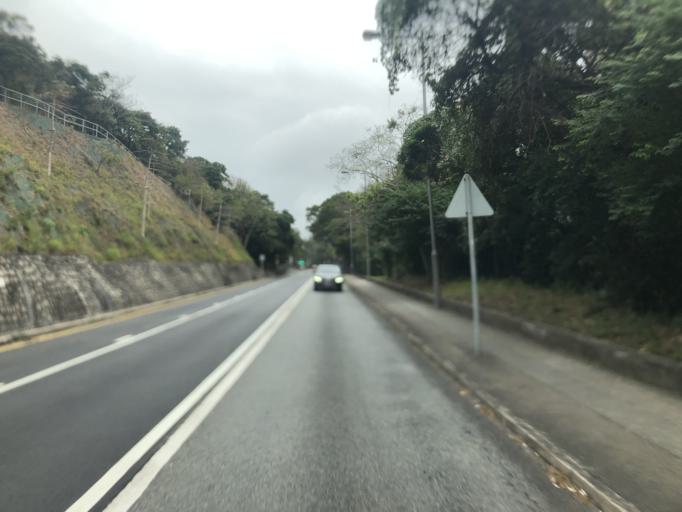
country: HK
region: Wong Tai Sin
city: Wong Tai Sin
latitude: 22.3337
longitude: 114.2193
